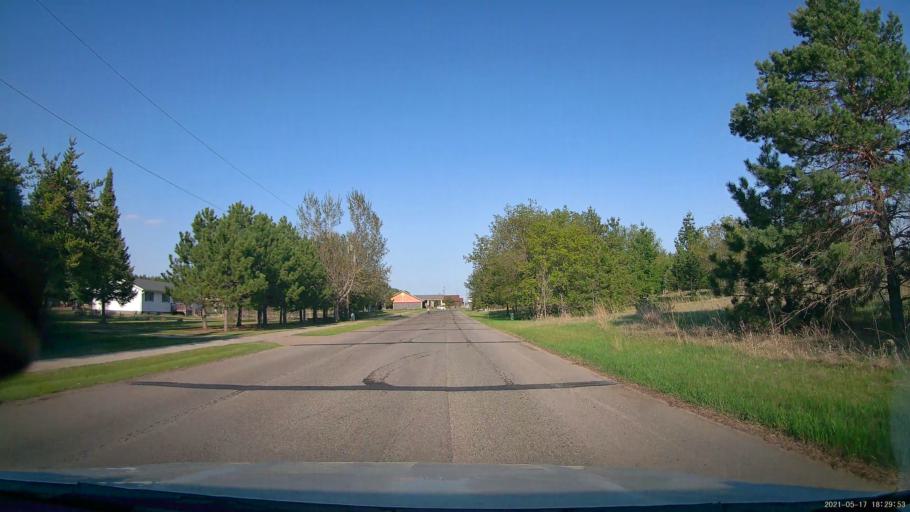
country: US
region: Minnesota
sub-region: Hubbard County
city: Park Rapids
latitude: 46.9252
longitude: -95.0444
